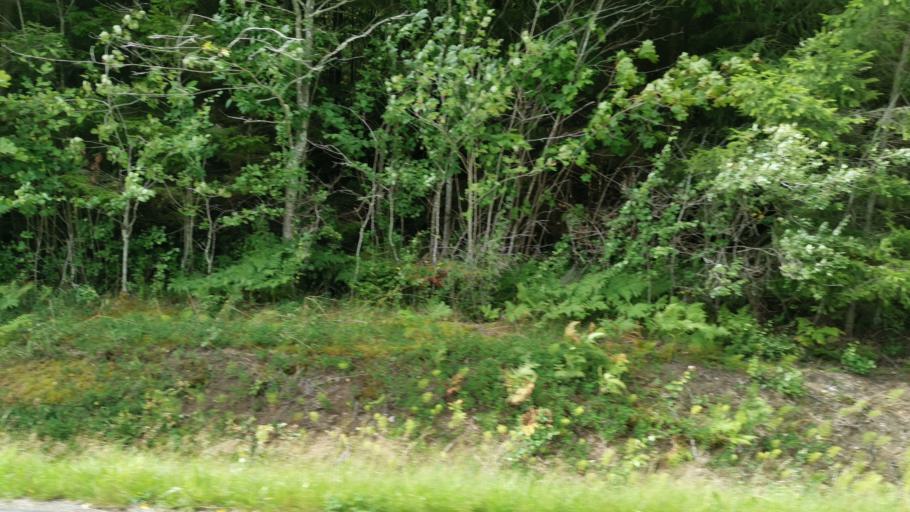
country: SE
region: Vaestra Goetaland
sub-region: Lysekils Kommun
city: Brastad
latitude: 58.4737
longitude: 11.4241
